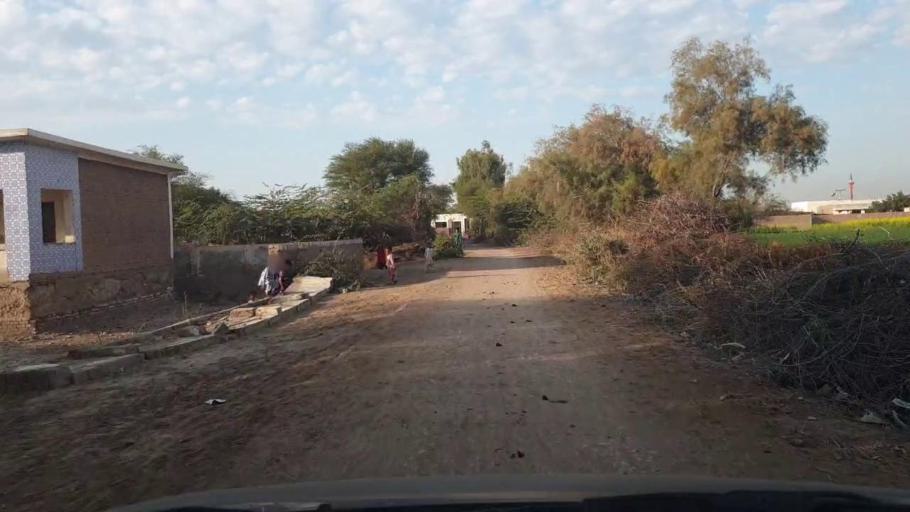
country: PK
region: Sindh
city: Sakrand
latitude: 26.0275
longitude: 68.3897
